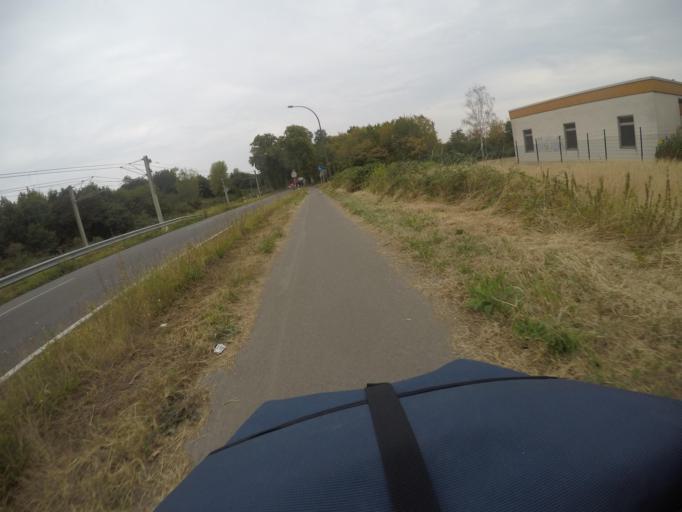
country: DE
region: North Rhine-Westphalia
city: Wesseling
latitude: 50.8095
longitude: 7.0034
